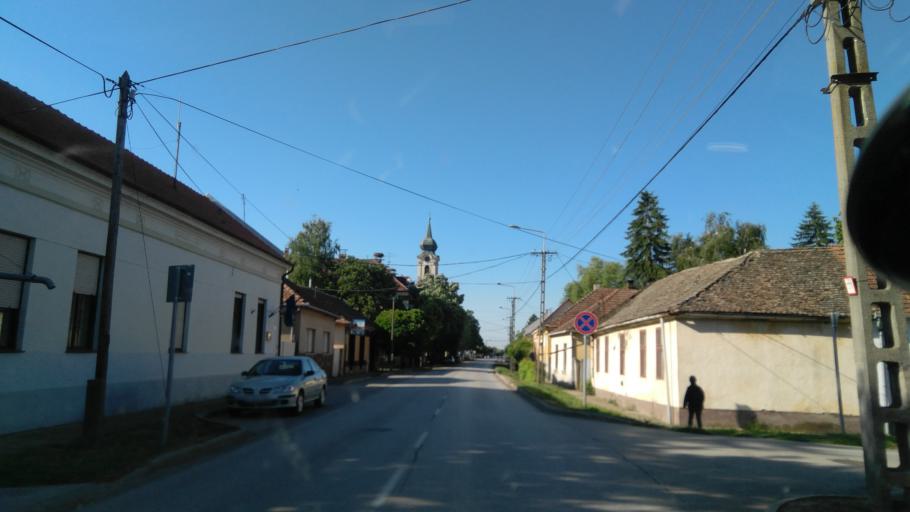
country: HU
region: Bekes
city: Elek
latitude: 46.5314
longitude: 21.2532
